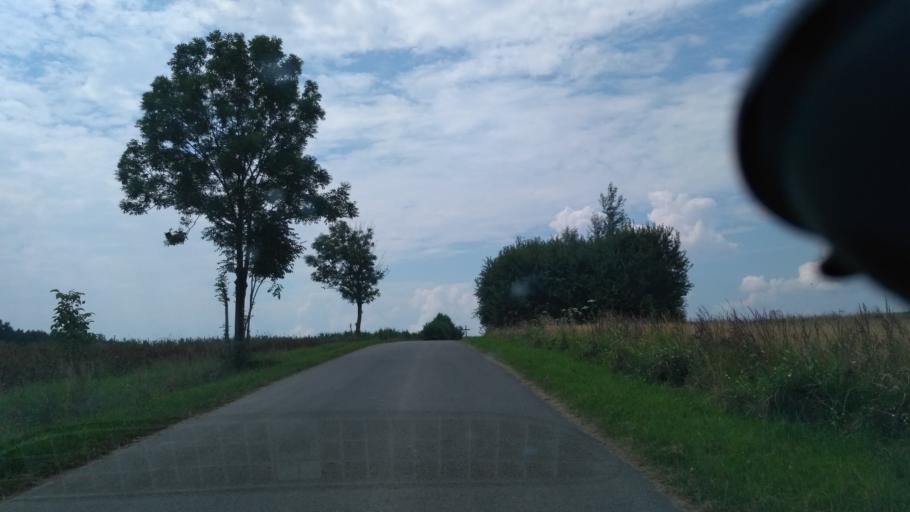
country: PL
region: Subcarpathian Voivodeship
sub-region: Powiat przeworski
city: Lopuszka Wielka
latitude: 49.9126
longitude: 22.3985
